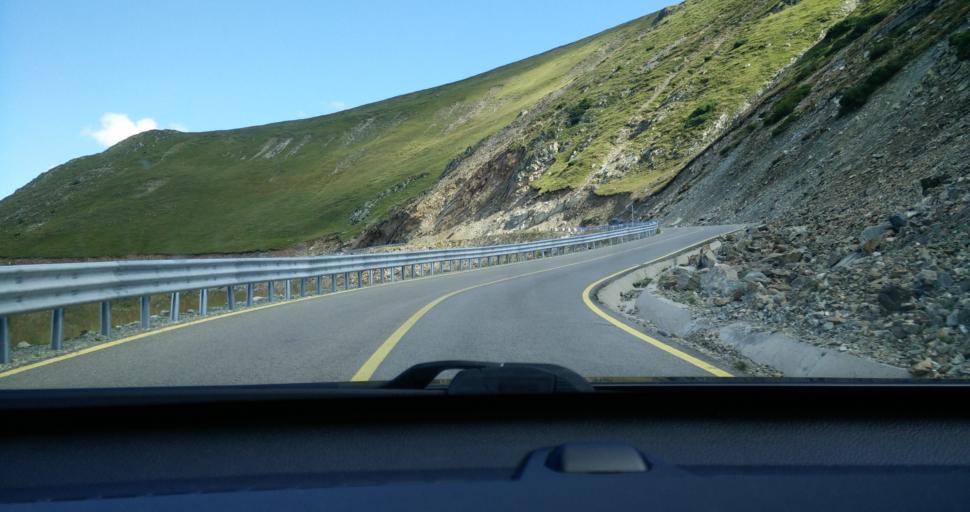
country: RO
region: Gorj
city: Novaci-Straini
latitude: 45.3251
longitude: 23.6822
